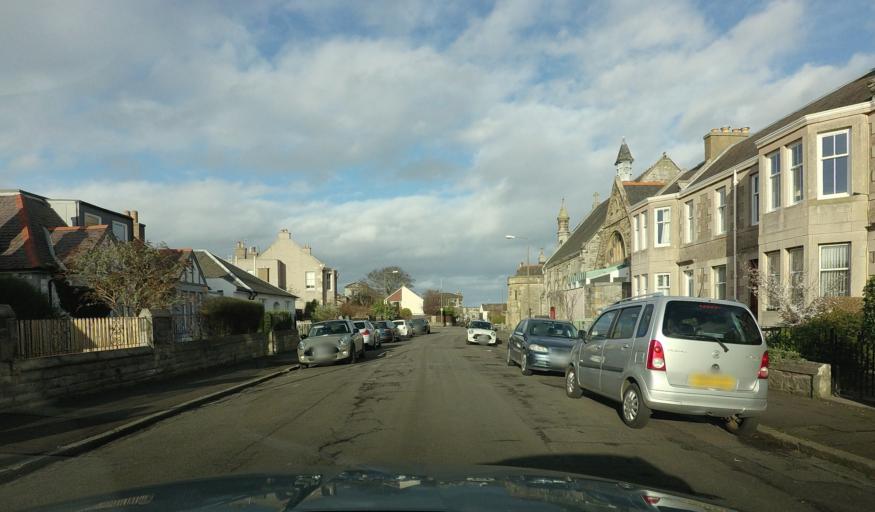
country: GB
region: Scotland
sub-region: Edinburgh
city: Edinburgh
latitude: 55.9785
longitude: -3.2113
